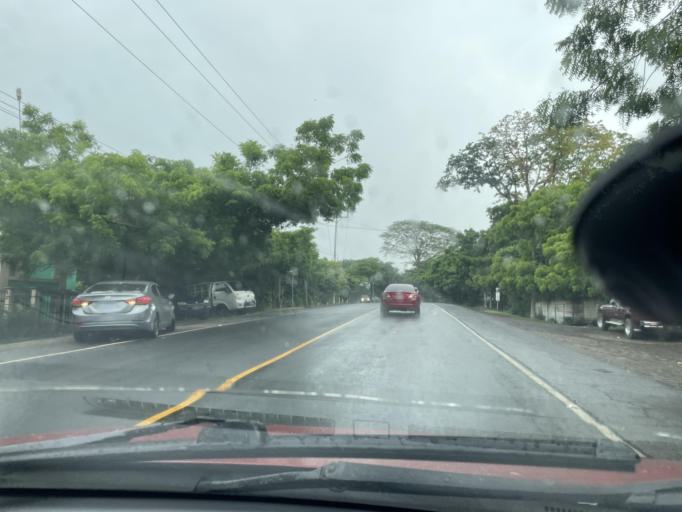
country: SV
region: San Miguel
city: San Miguel
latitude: 13.5593
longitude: -88.1087
